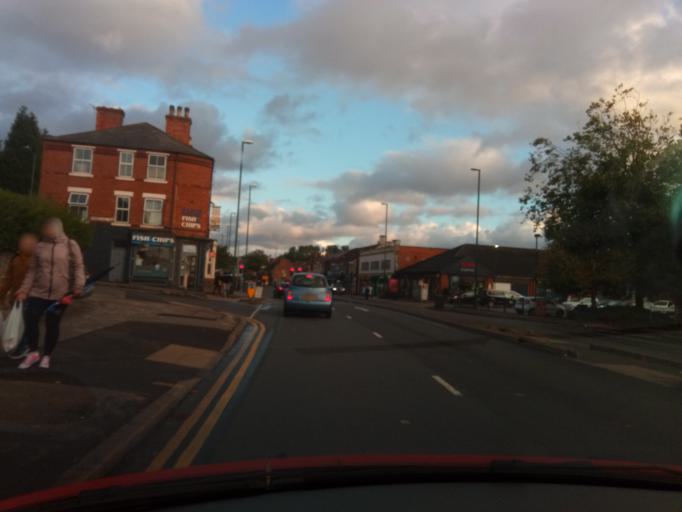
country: GB
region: England
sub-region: Nottingham
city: Nottingham
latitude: 52.9648
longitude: -1.1804
